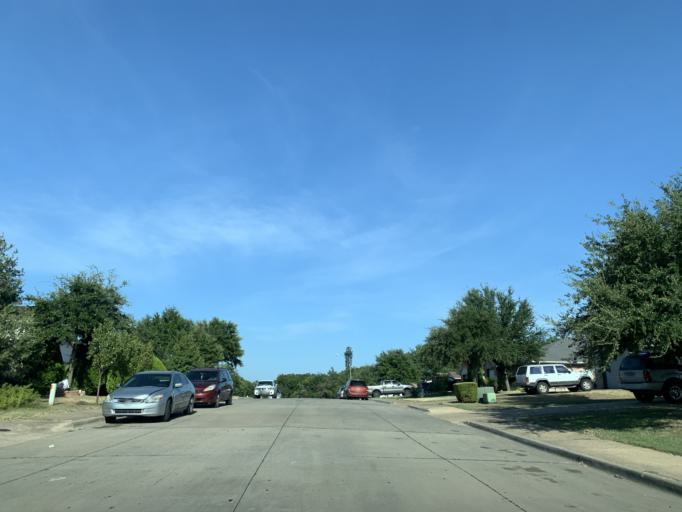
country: US
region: Texas
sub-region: Dallas County
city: Cockrell Hill
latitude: 32.7075
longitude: -96.8859
